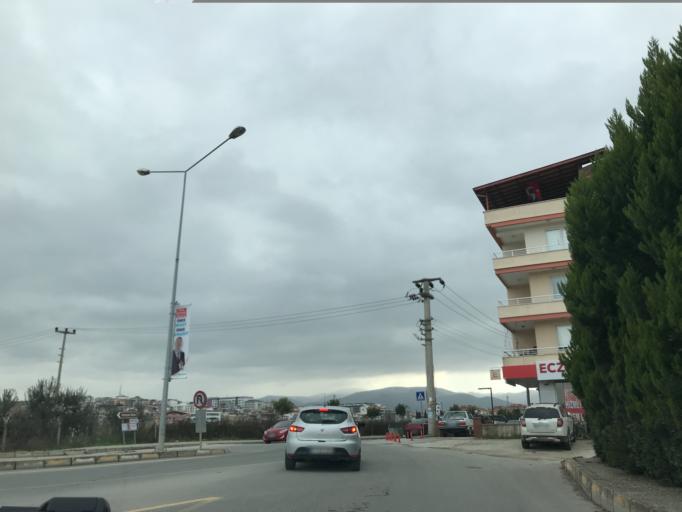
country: TR
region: Yalova
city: Ciftlikkoy
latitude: 40.6610
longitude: 29.3061
